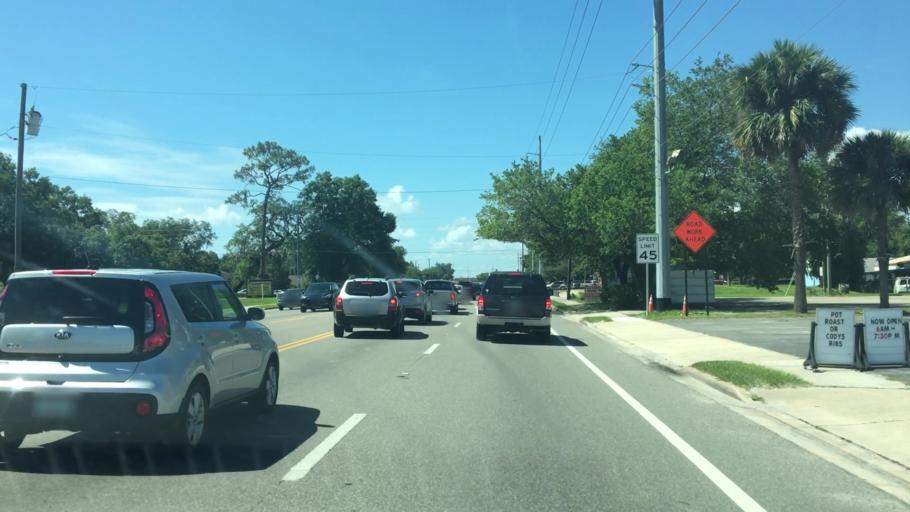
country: US
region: Florida
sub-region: Volusia County
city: Orange City
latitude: 28.9326
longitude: -81.2990
